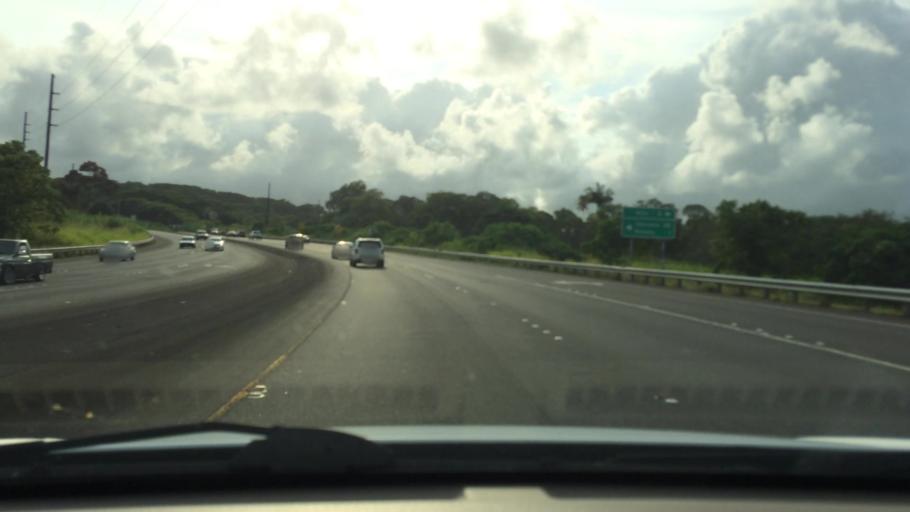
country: US
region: Hawaii
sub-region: Hawaii County
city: Kea'au
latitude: 19.6329
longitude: -155.0367
